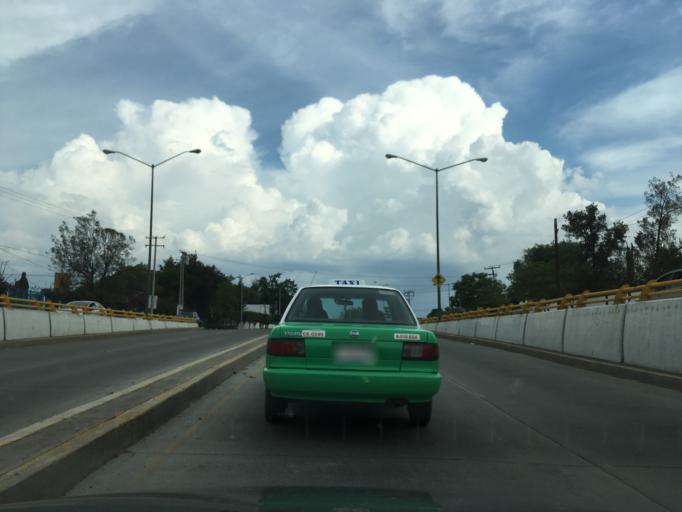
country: MX
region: Guanajuato
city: Celaya
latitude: 20.5349
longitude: -100.8194
